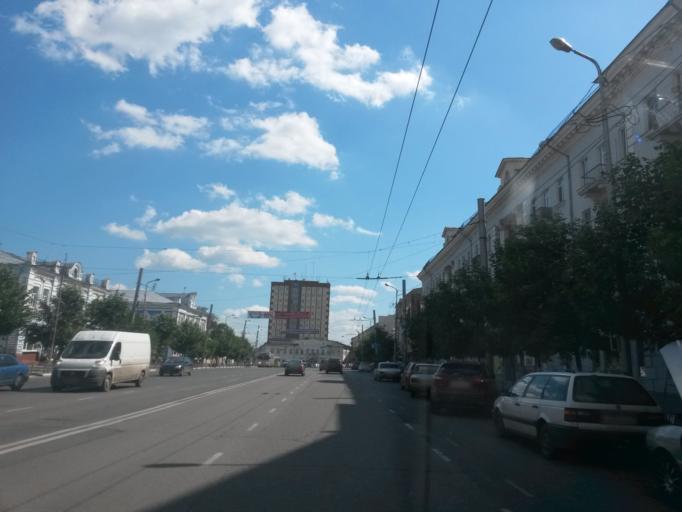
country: RU
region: Ivanovo
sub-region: Gorod Ivanovo
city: Ivanovo
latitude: 56.9968
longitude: 40.9769
